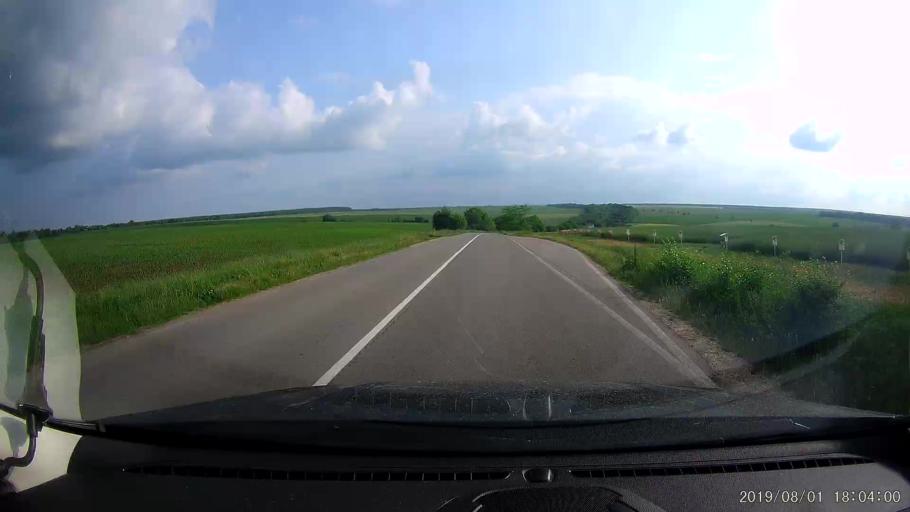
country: BG
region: Silistra
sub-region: Obshtina Alfatar
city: Alfatar
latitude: 43.9153
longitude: 27.2892
